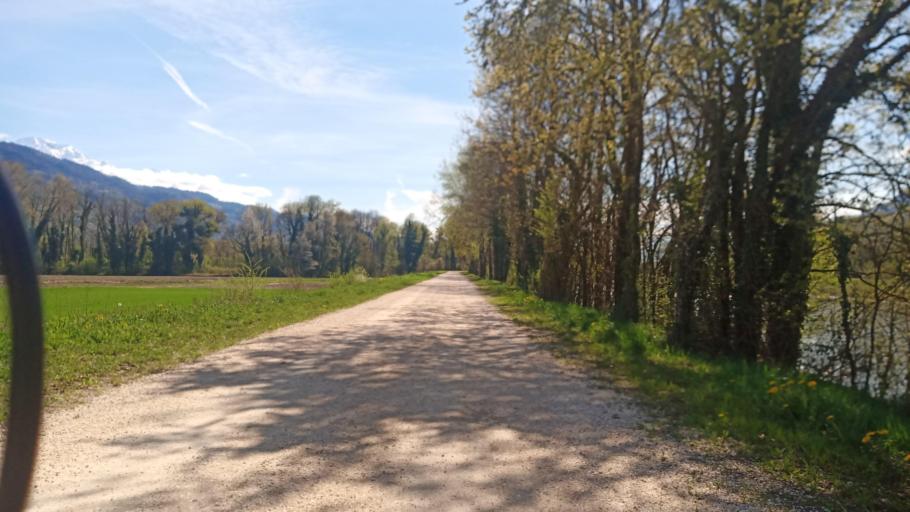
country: FR
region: Rhone-Alpes
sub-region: Departement de l'Isere
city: Tencin
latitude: 45.3248
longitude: 5.9580
